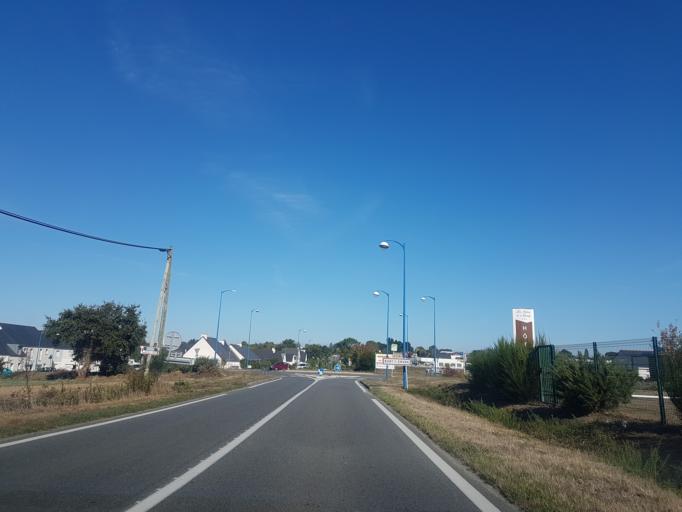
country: FR
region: Pays de la Loire
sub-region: Departement de la Loire-Atlantique
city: Nort-sur-Erdre
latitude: 47.4357
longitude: -1.4829
